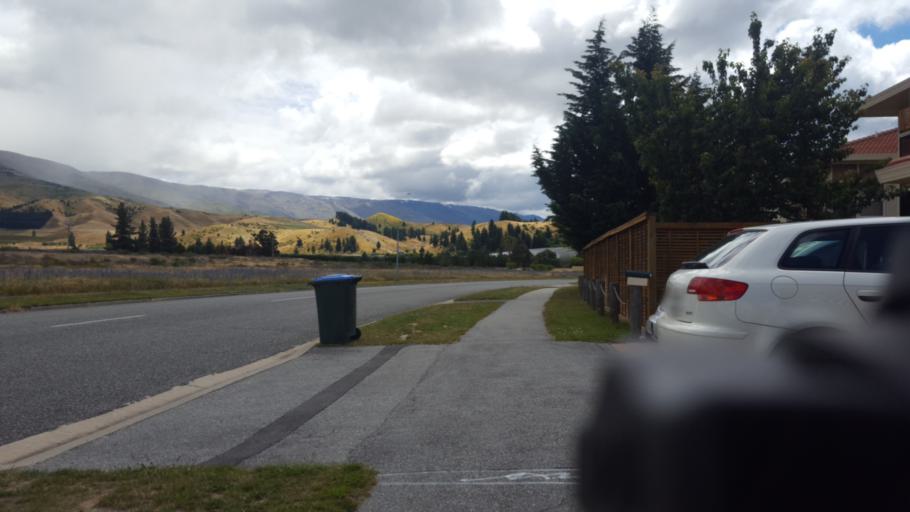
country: NZ
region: Otago
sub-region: Queenstown-Lakes District
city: Wanaka
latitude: -45.0432
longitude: 169.1798
